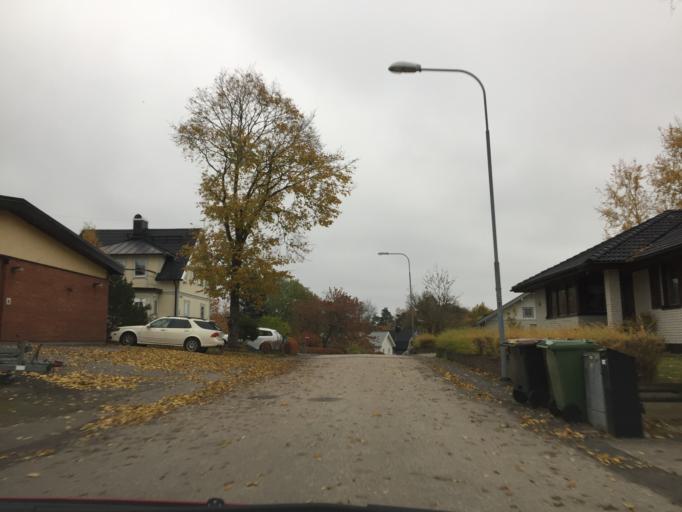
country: SE
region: Vaestra Goetaland
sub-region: Trollhattan
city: Trollhattan
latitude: 58.2681
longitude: 12.2784
